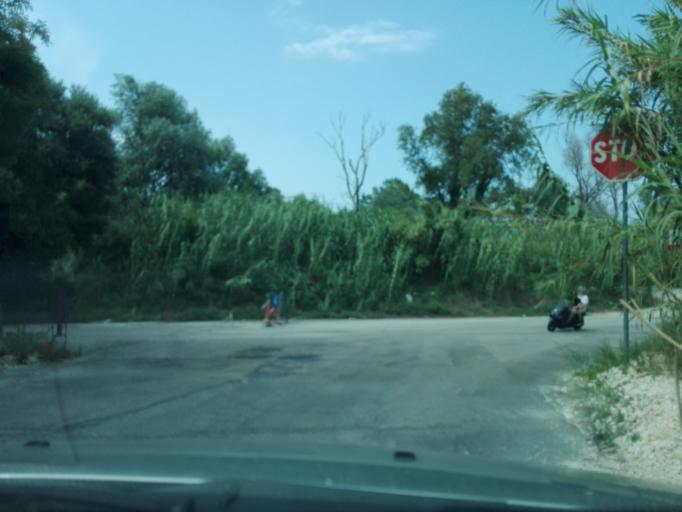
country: IT
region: Abruzzo
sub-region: Provincia di Pescara
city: Montesilvano Marina
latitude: 42.5087
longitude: 14.1285
